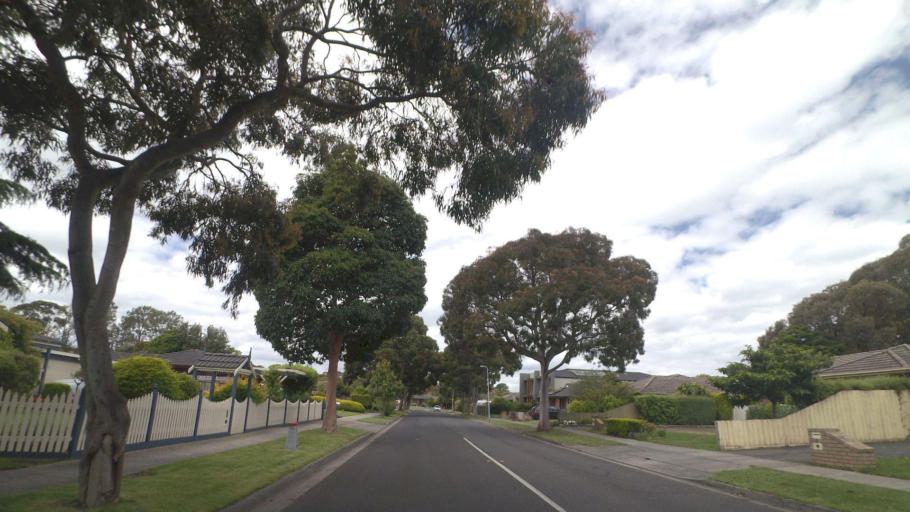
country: AU
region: Victoria
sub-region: Knox
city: Knoxfield
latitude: -37.8751
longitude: 145.2360
